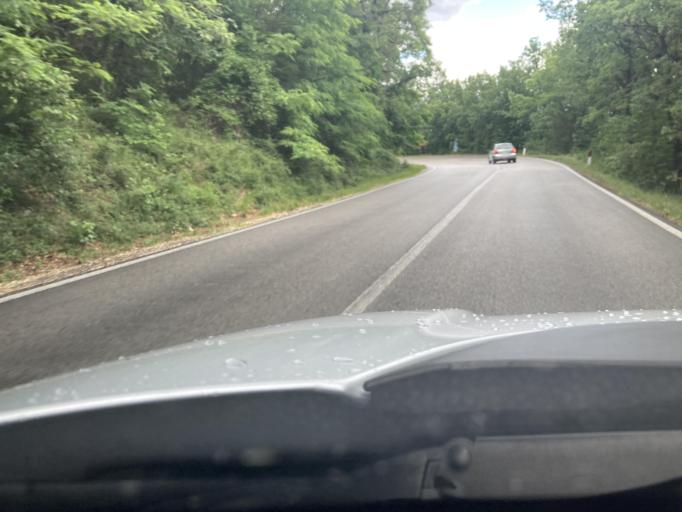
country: IT
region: Abruzzo
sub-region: Provincia dell' Aquila
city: San Panfilo d'Ocre
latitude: 42.2801
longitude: 13.4594
